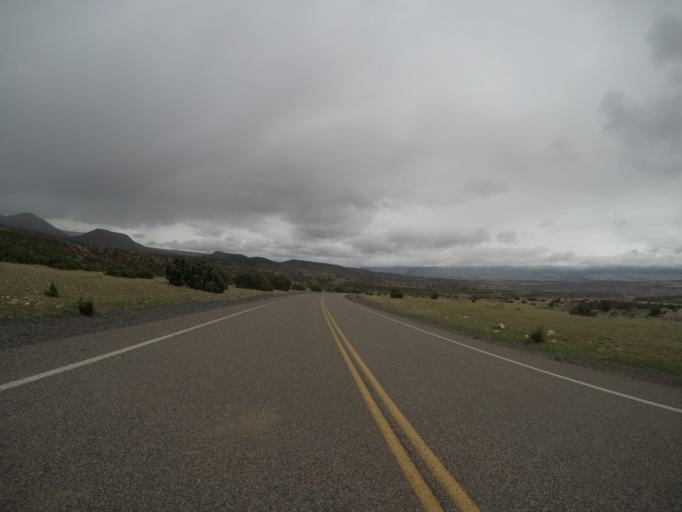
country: US
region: Wyoming
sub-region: Big Horn County
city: Lovell
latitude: 45.0977
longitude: -108.2486
